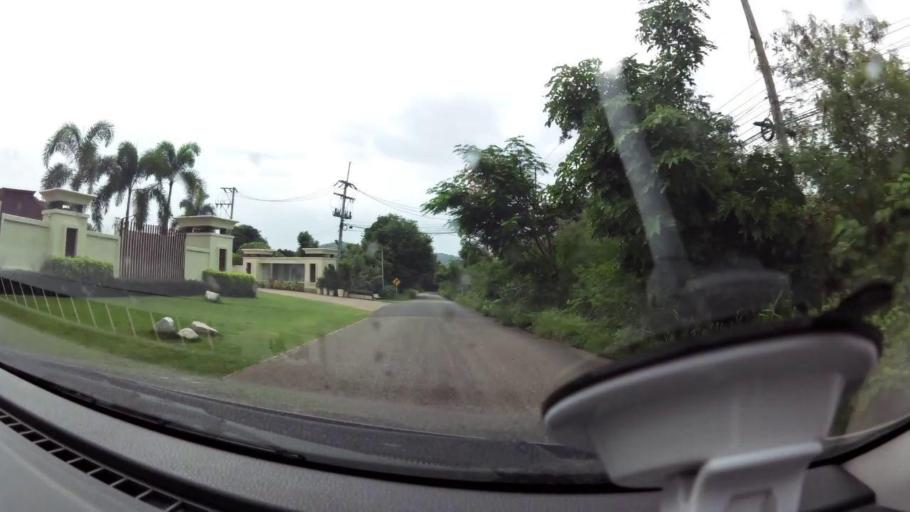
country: TH
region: Prachuap Khiri Khan
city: Pran Buri
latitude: 12.4402
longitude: 99.9704
